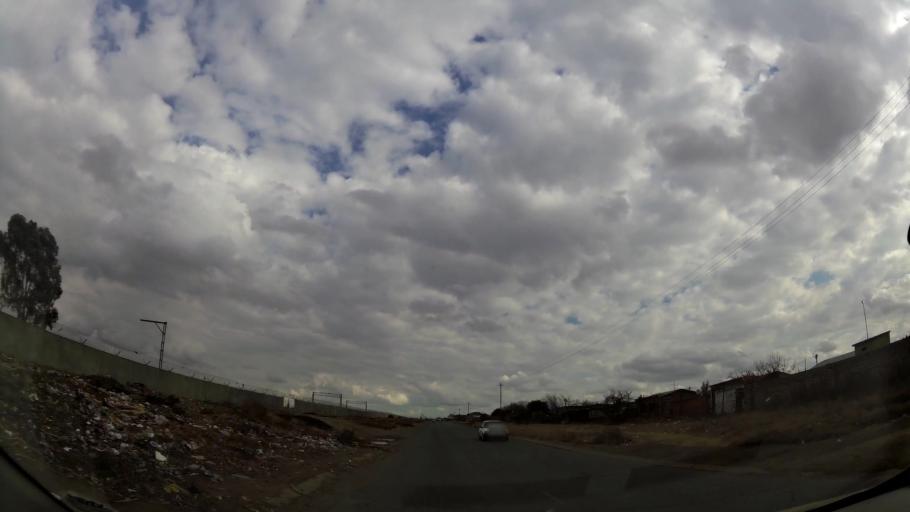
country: ZA
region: Orange Free State
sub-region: Fezile Dabi District Municipality
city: Sasolburg
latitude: -26.8590
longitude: 27.8608
